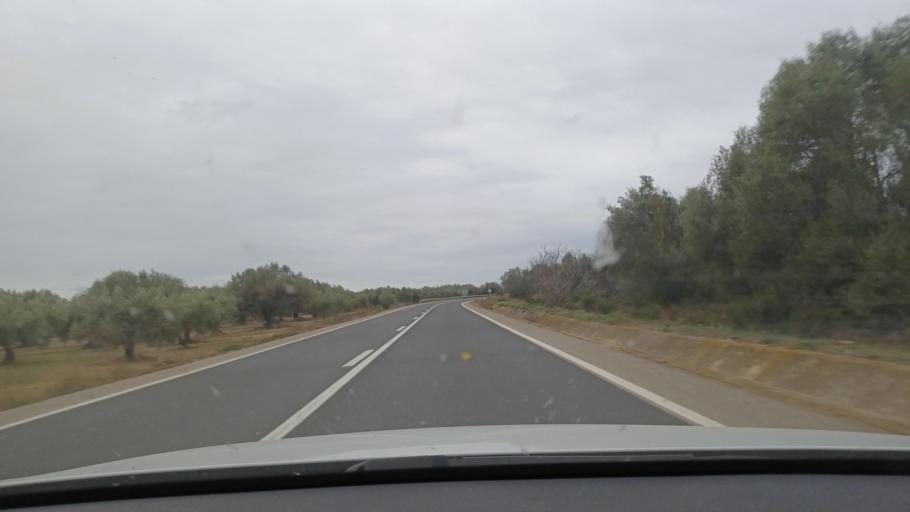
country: ES
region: Catalonia
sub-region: Provincia de Tarragona
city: Ulldecona
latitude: 40.6446
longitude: 0.3809
